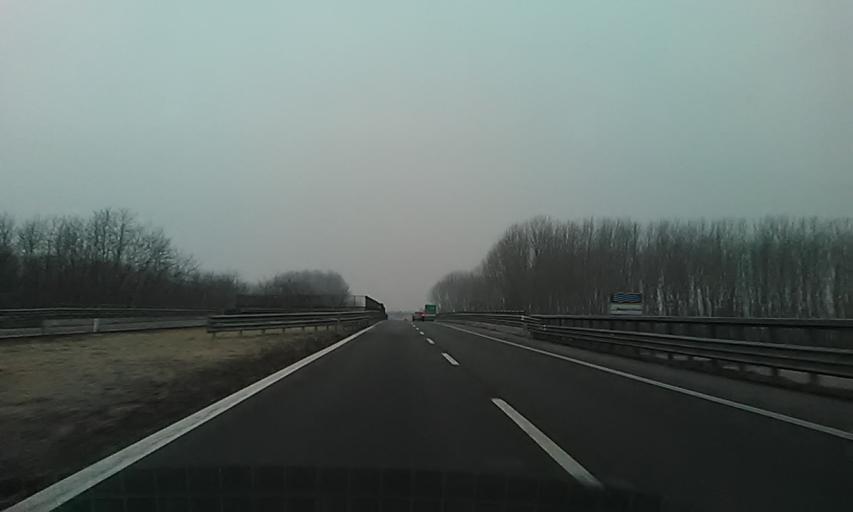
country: IT
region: Piedmont
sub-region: Provincia di Torino
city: Caravino
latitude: 45.4185
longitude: 7.9632
